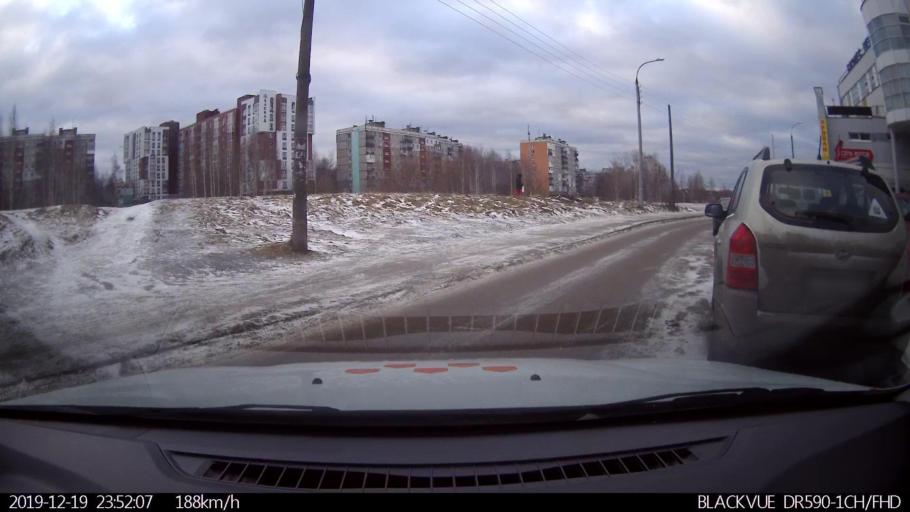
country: RU
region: Vologda
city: Molochnoye
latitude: 58.9947
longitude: 39.4860
